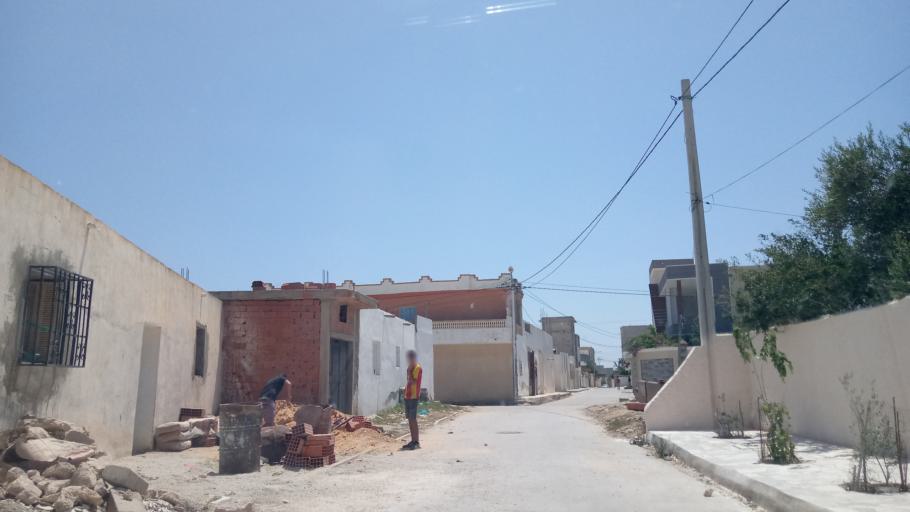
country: TN
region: Al Qayrawan
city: Sbikha
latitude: 36.1192
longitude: 10.0902
